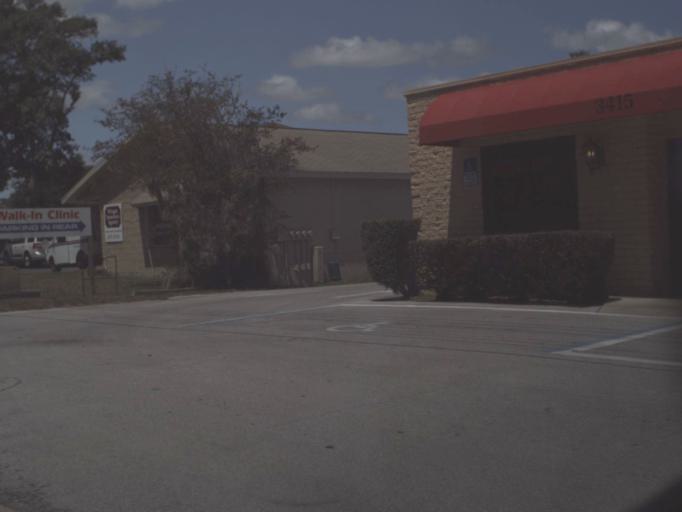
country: US
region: Florida
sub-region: Marion County
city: Ocala
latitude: 29.1960
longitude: -82.0895
